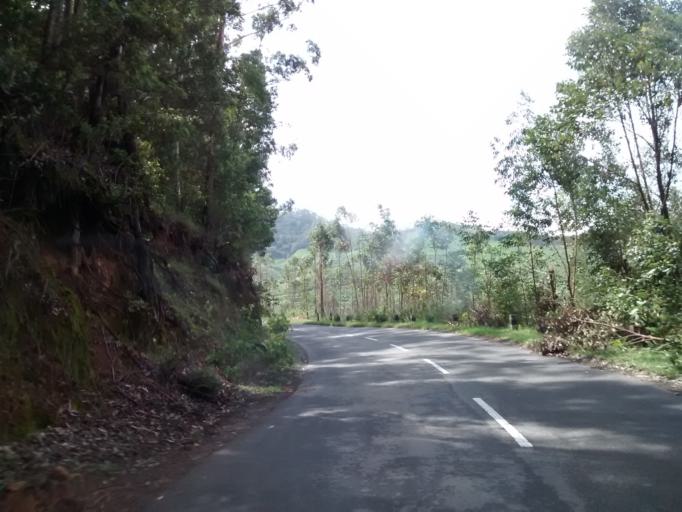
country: IN
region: Kerala
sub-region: Idukki
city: Munnar
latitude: 10.0990
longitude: 77.1129
